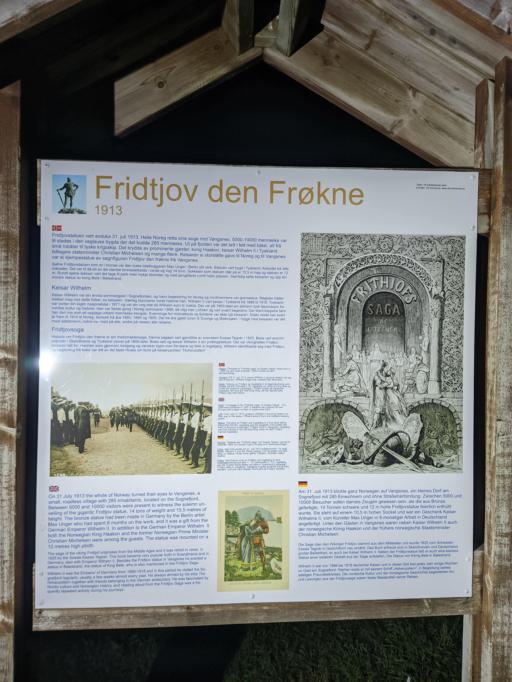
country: NO
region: Sogn og Fjordane
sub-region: Vik
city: Vikoyri
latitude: 61.1721
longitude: 6.6406
